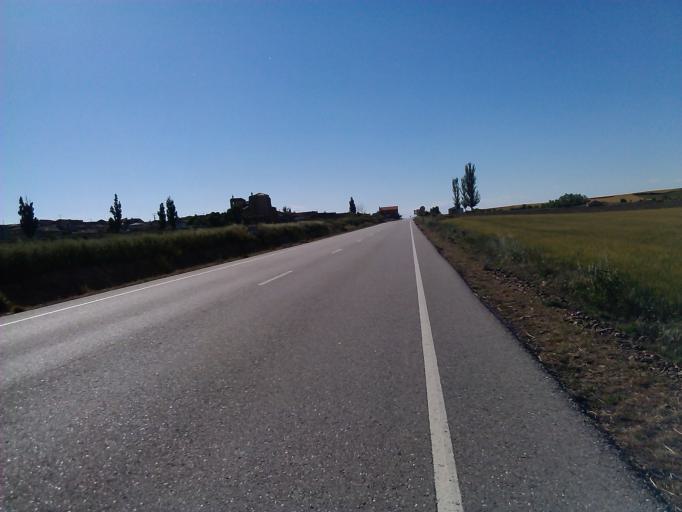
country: ES
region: Castille and Leon
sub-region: Provincia de Burgos
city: Pedrosa del Principe
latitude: 42.3069
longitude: -4.1676
